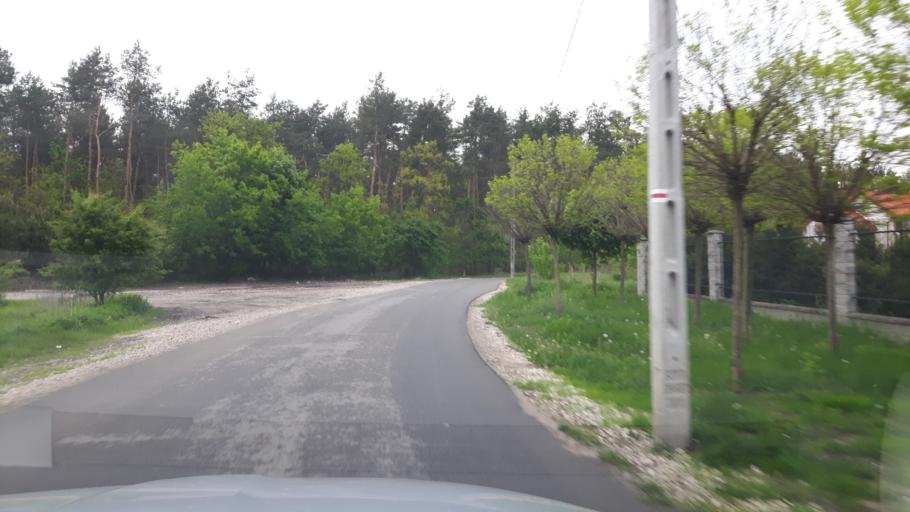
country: PL
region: Masovian Voivodeship
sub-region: Warszawa
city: Rembertow
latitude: 52.2764
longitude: 21.1473
